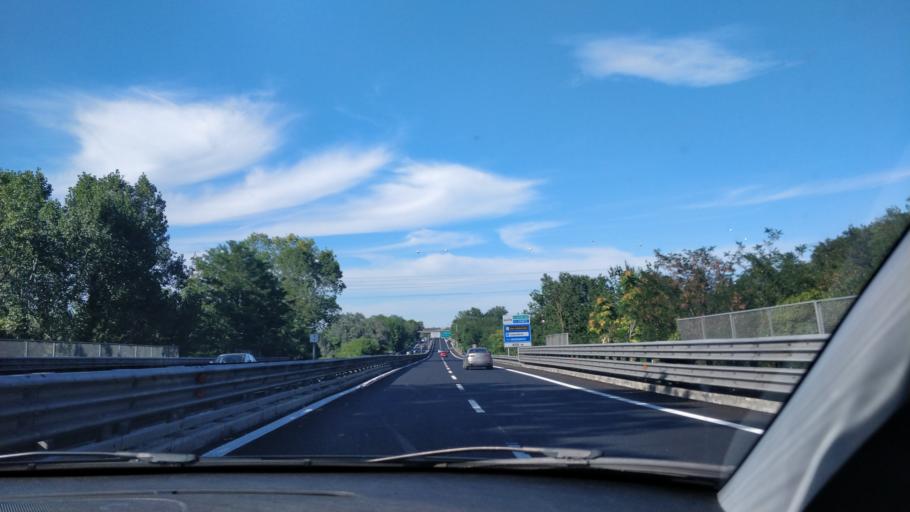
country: IT
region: Abruzzo
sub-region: Provincia di Chieti
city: Chieti
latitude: 42.3905
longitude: 14.1551
